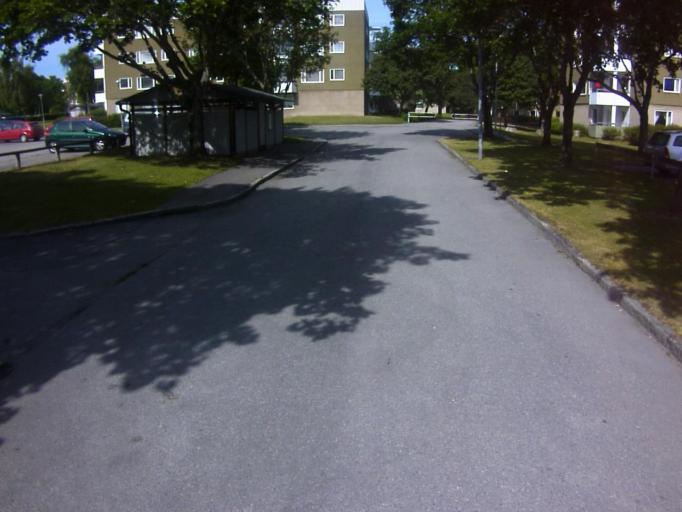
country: SE
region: Soedermanland
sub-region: Eskilstuna Kommun
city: Eskilstuna
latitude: 59.3519
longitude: 16.5322
